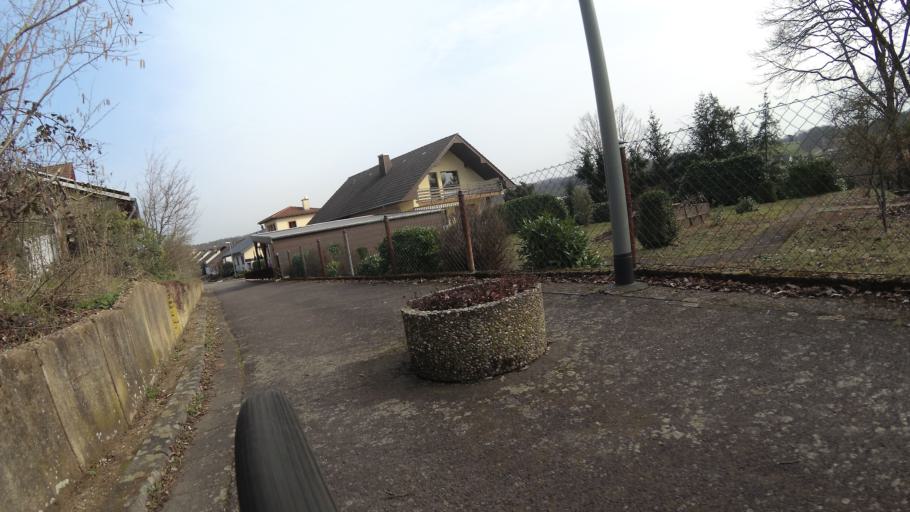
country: DE
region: Saarland
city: Losheim
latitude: 49.4557
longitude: 6.7817
